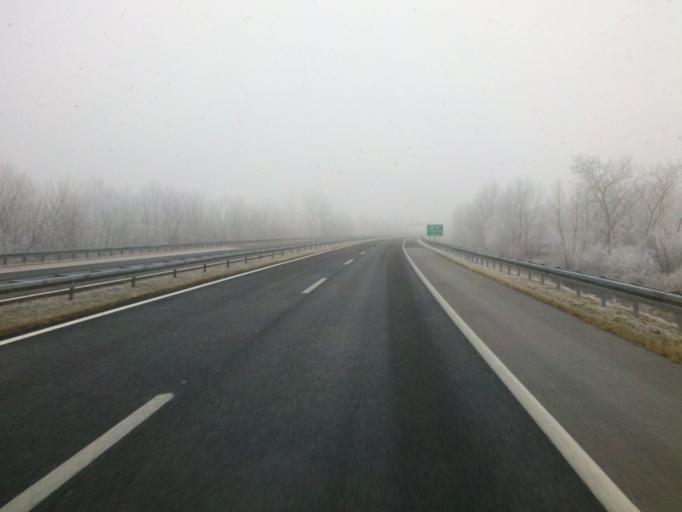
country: HR
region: Medimurska
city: Orehovica
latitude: 46.3049
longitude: 16.5040
